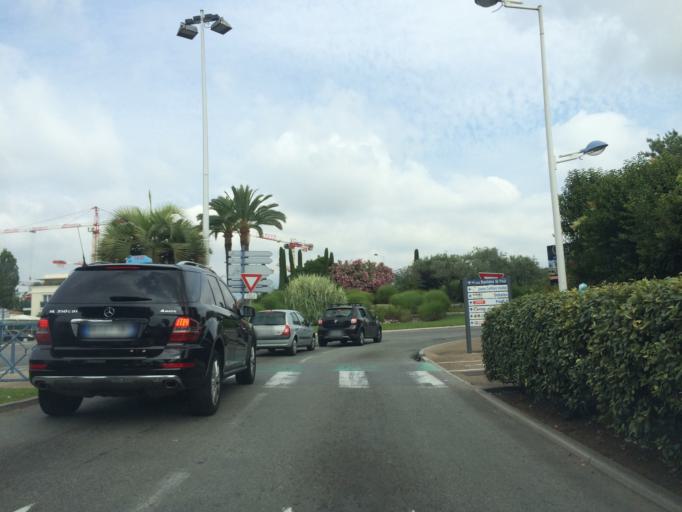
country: FR
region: Provence-Alpes-Cote d'Azur
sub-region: Departement des Alpes-Maritimes
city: Villeneuve-Loubet
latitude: 43.6623
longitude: 7.1324
